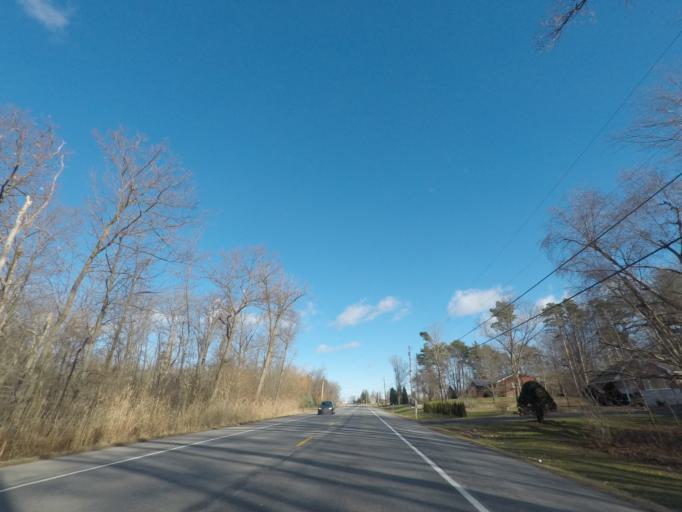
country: US
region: New York
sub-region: Saratoga County
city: Mechanicville
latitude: 42.8499
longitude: -73.7295
